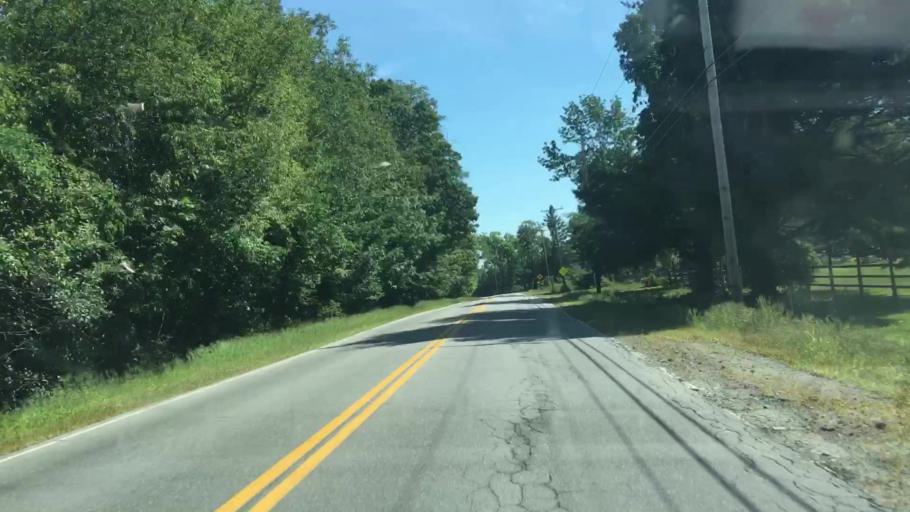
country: US
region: Maine
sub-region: Penobscot County
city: Bradford
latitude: 45.1721
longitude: -68.8507
